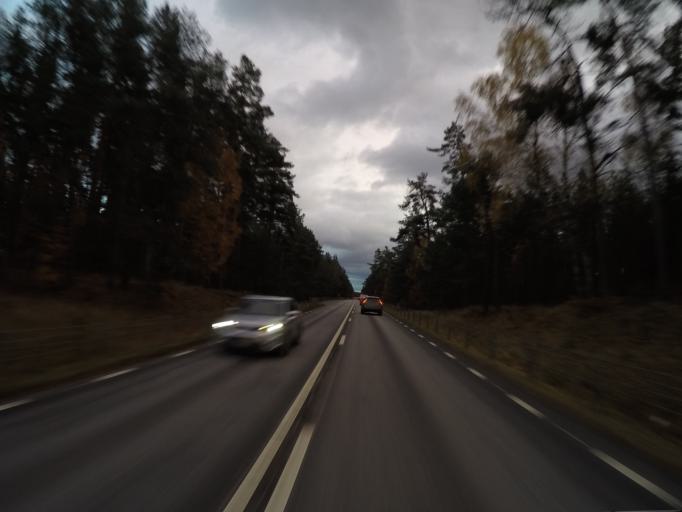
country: SE
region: Skane
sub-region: Kristianstads Kommun
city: Degeberga
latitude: 55.8576
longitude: 14.0918
